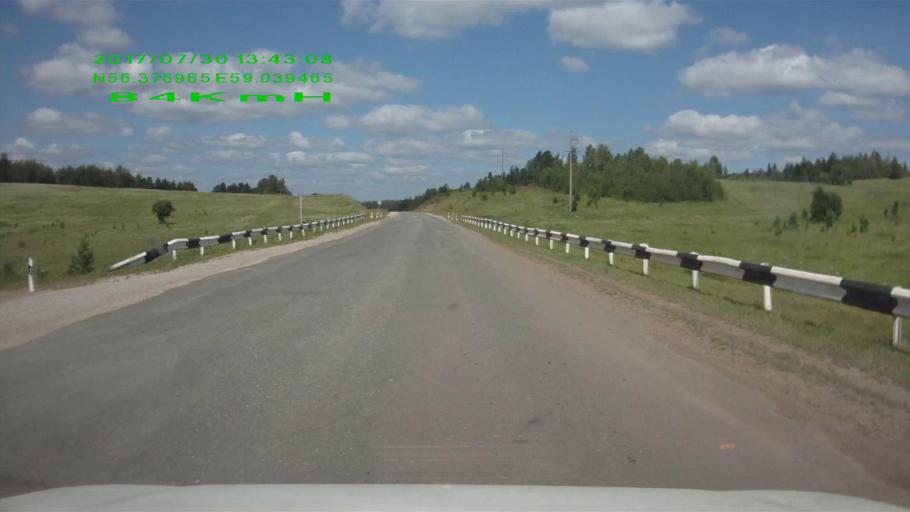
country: RU
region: Sverdlovsk
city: Mikhaylovsk
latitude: 56.3773
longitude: 59.0395
